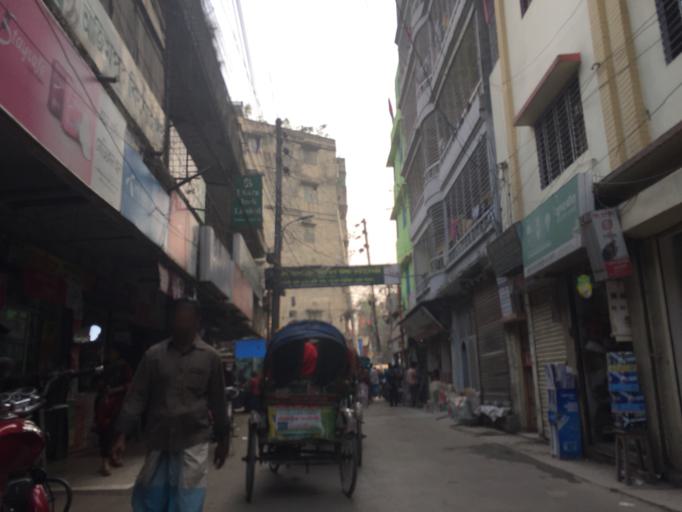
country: BD
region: Dhaka
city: Azimpur
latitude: 23.7269
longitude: 90.3817
